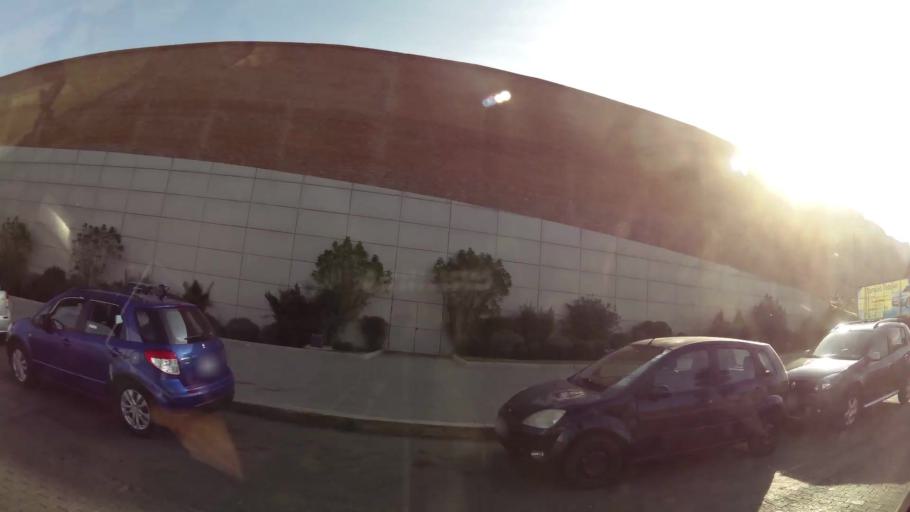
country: BO
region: La Paz
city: La Paz
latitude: -16.5318
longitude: -68.0869
